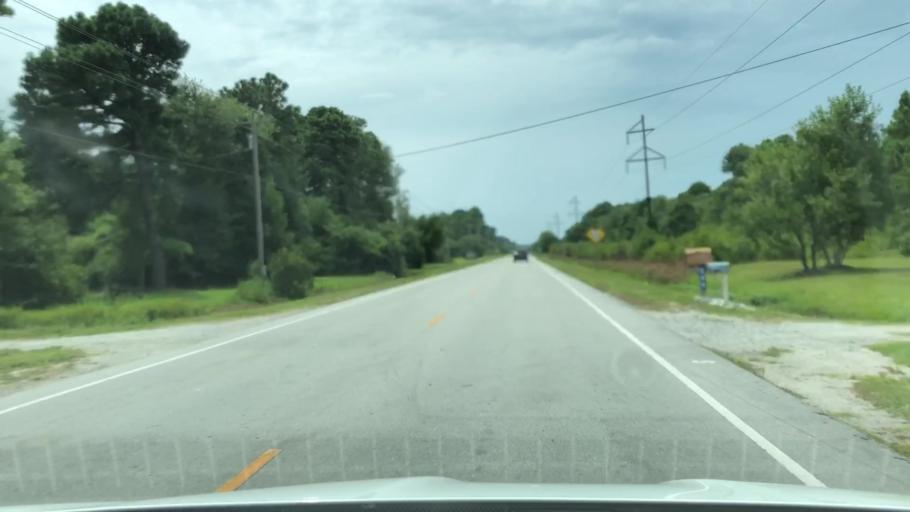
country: US
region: North Carolina
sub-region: Carteret County
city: Newport
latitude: 34.7485
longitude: -76.8792
